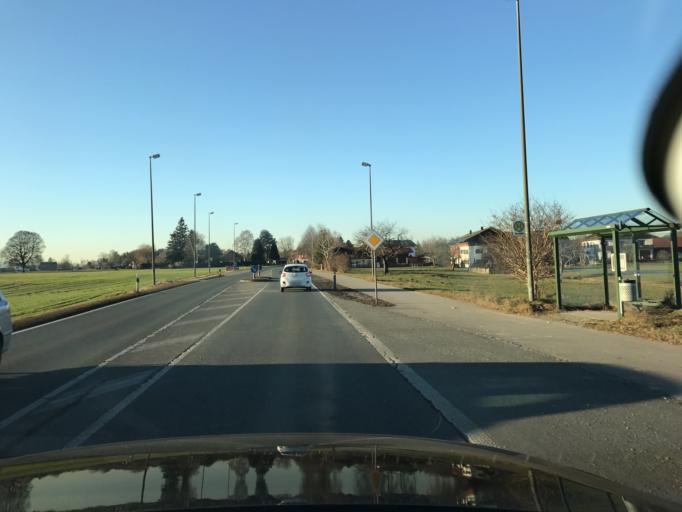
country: DE
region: Bavaria
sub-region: Upper Bavaria
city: Bad Aibling
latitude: 47.8459
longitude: 12.0223
